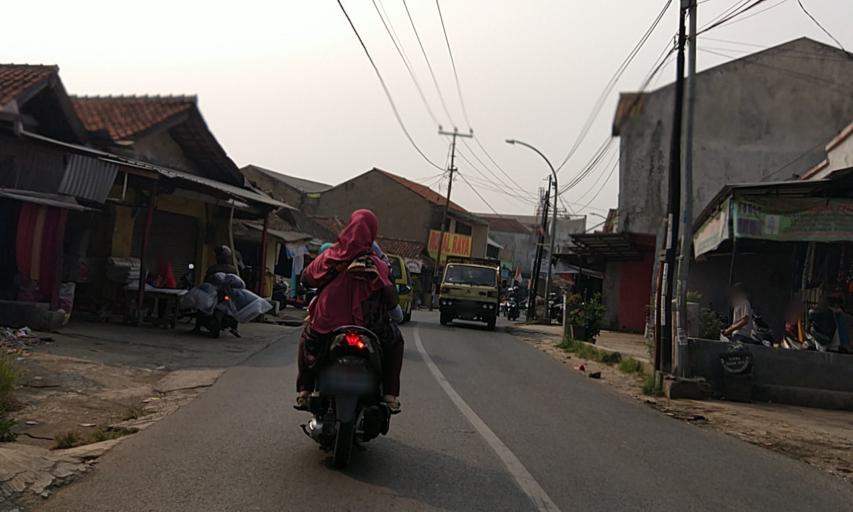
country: ID
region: West Java
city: Margahayukencana
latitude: -6.9472
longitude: 107.5645
